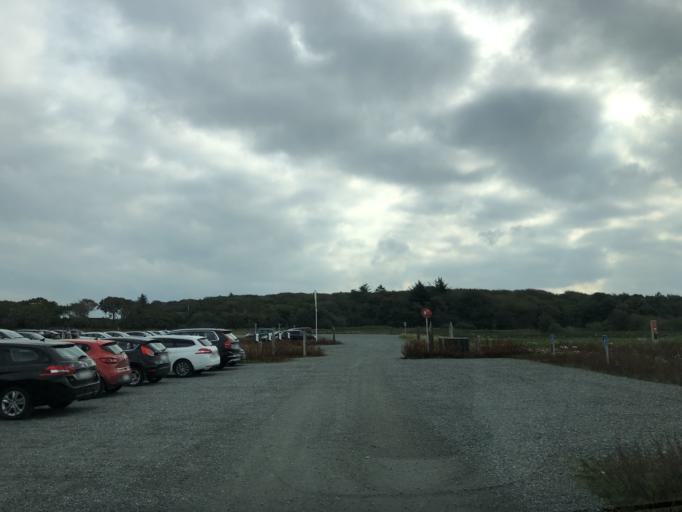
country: DK
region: Central Jutland
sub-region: Ringkobing-Skjern Kommune
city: Ringkobing
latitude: 56.1025
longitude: 8.2465
